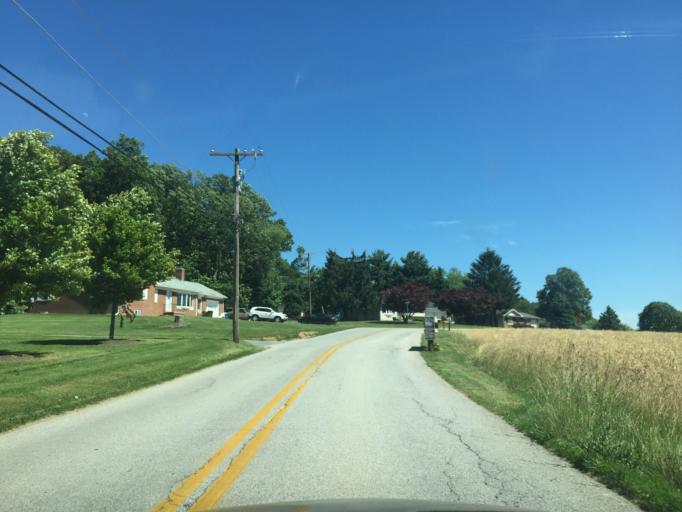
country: US
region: Maryland
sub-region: Carroll County
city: Manchester
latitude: 39.6269
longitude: -76.9308
